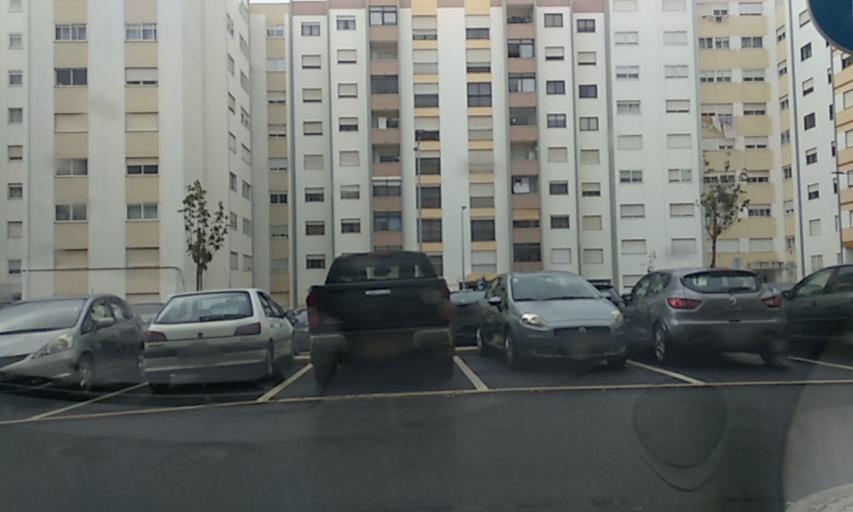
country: PT
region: Lisbon
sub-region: Sintra
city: Cacem
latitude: 38.7554
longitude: -9.2874
